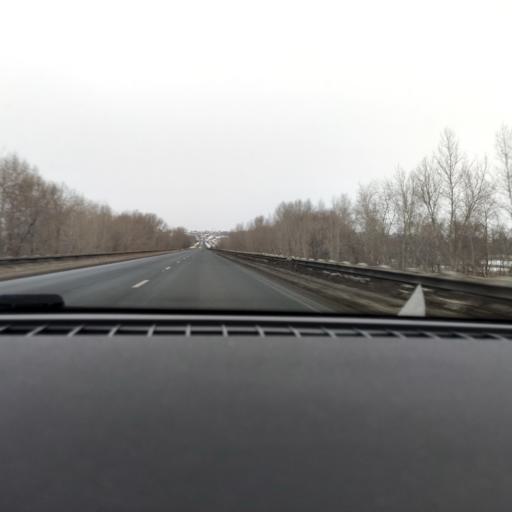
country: RU
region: Samara
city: Smyshlyayevka
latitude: 53.2239
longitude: 50.4968
